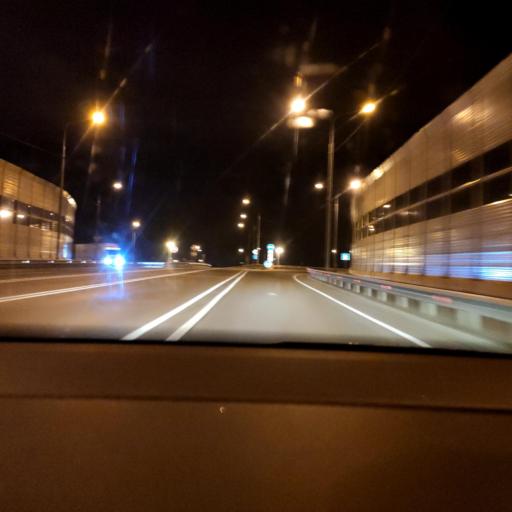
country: RU
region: Moskovskaya
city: Bolshevo
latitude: 55.9512
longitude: 37.8288
